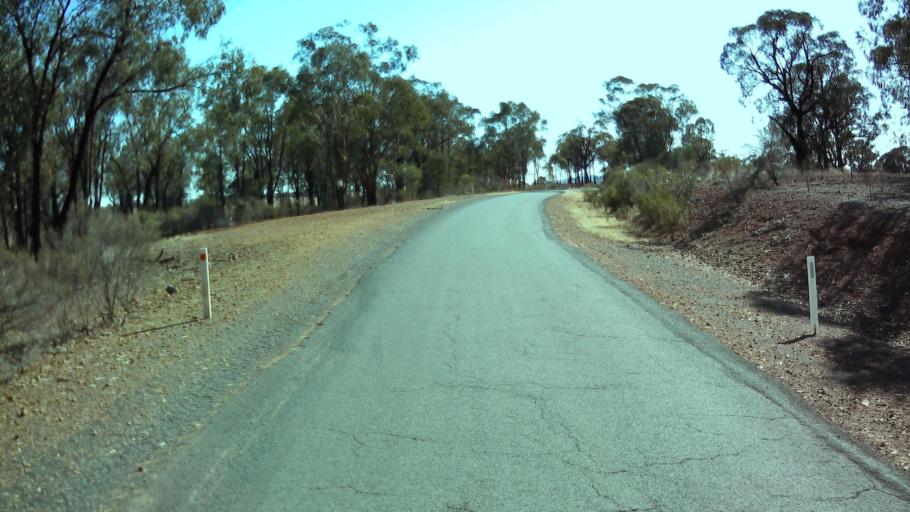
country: AU
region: New South Wales
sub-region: Weddin
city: Grenfell
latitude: -33.7833
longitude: 147.9598
